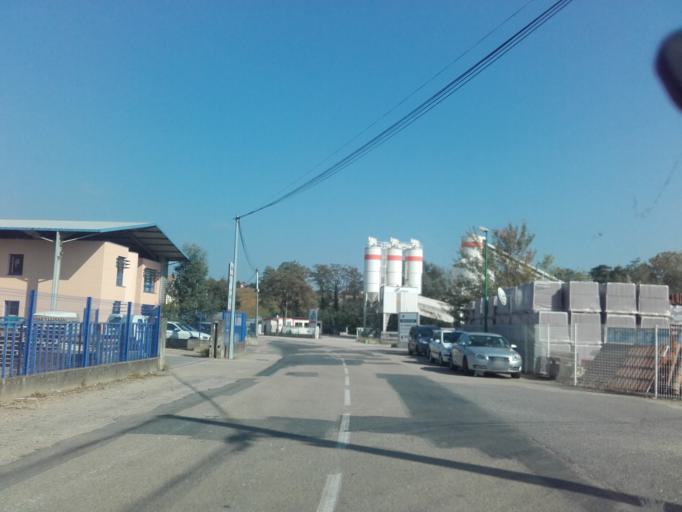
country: FR
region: Bourgogne
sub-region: Departement de Saone-et-Loire
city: La Chapelle-de-Guinchay
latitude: 46.2193
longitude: 4.7438
